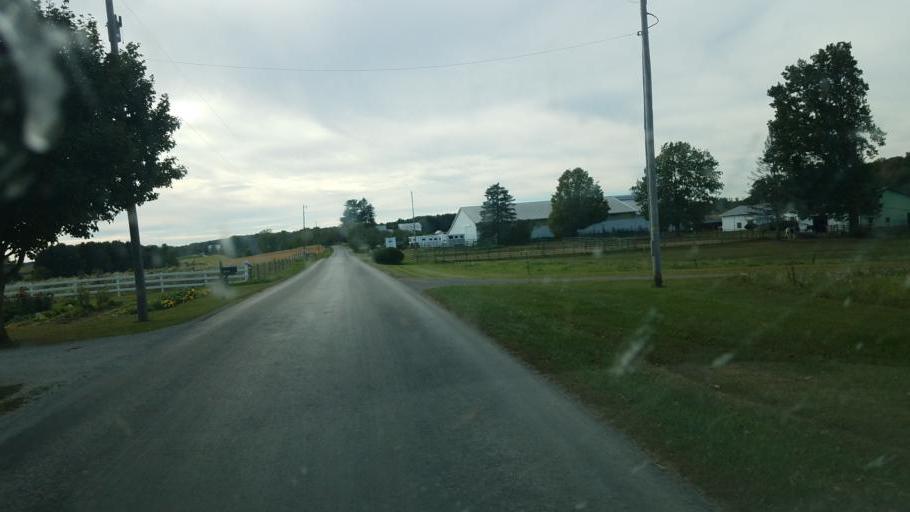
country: US
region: Ohio
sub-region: Knox County
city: Fredericktown
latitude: 40.5251
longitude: -82.6029
